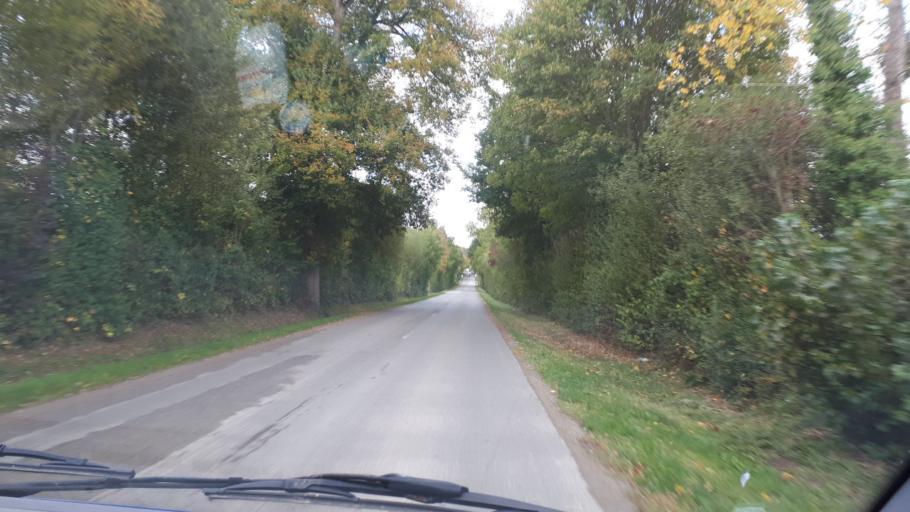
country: FR
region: Centre
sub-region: Departement d'Eure-et-Loir
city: Authon-du-Perche
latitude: 48.2297
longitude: 0.8665
